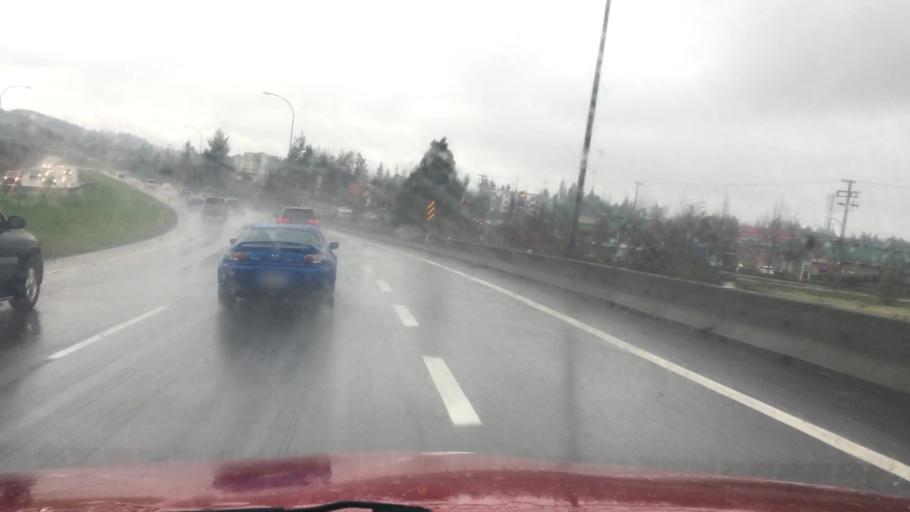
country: CA
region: British Columbia
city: Victoria
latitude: 48.4938
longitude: -123.3869
